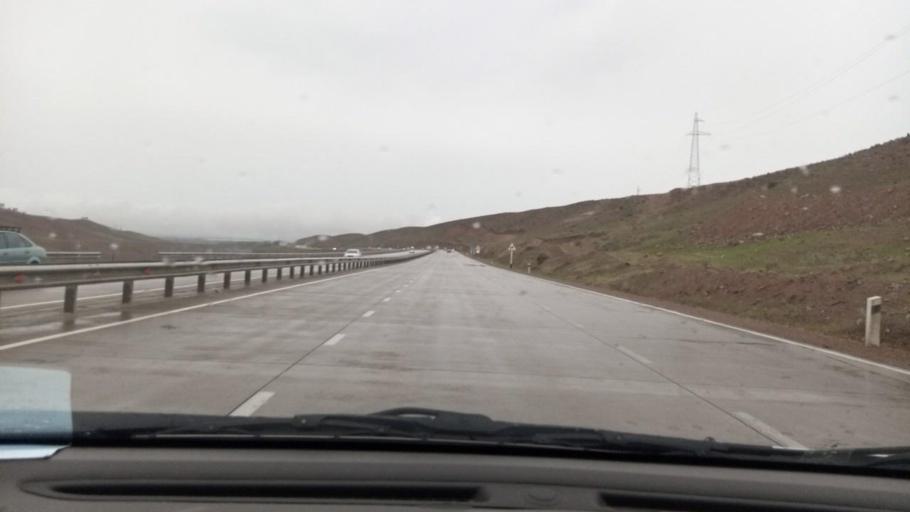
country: UZ
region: Namangan
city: Pop Shahri
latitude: 40.9336
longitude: 70.6988
